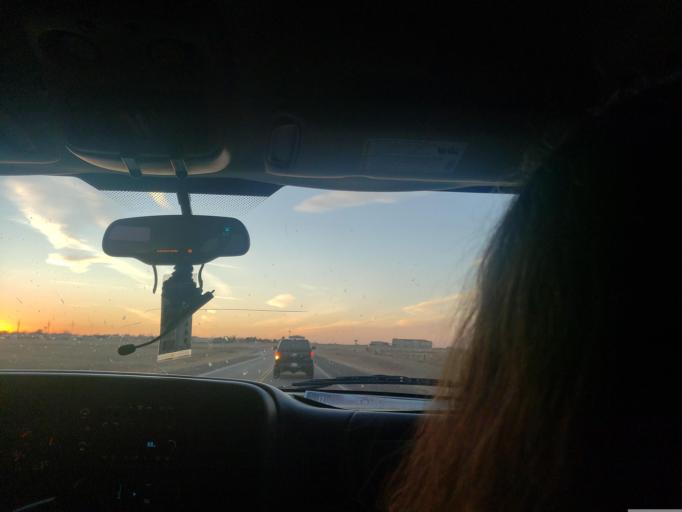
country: US
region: Kansas
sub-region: Seward County
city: Liberal
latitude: 37.0706
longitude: -100.9113
